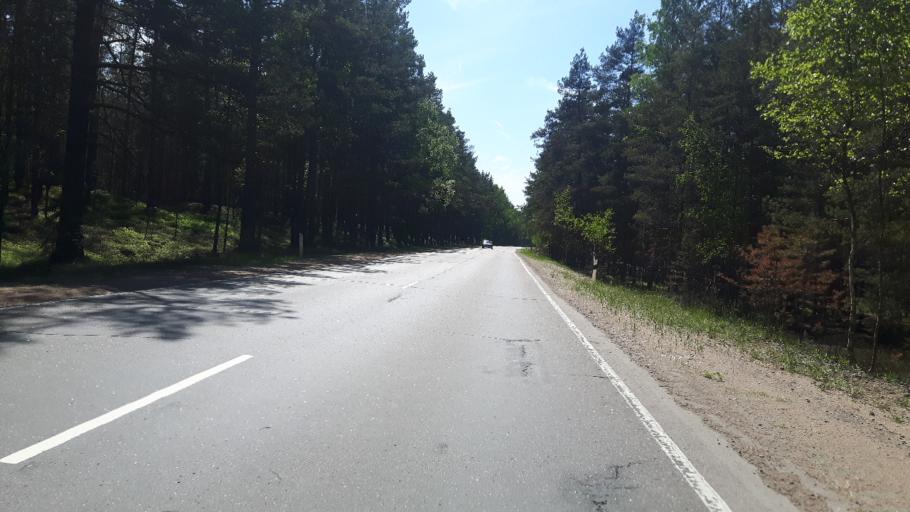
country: RU
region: Leningrad
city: Sista-Palkino
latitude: 59.7747
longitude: 28.8554
